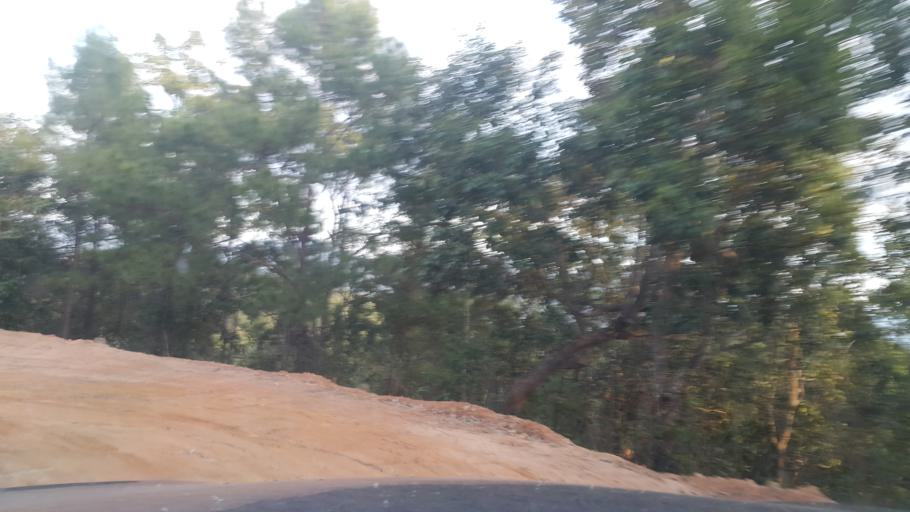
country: TH
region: Chiang Mai
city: Samoeng
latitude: 19.0061
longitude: 98.6607
